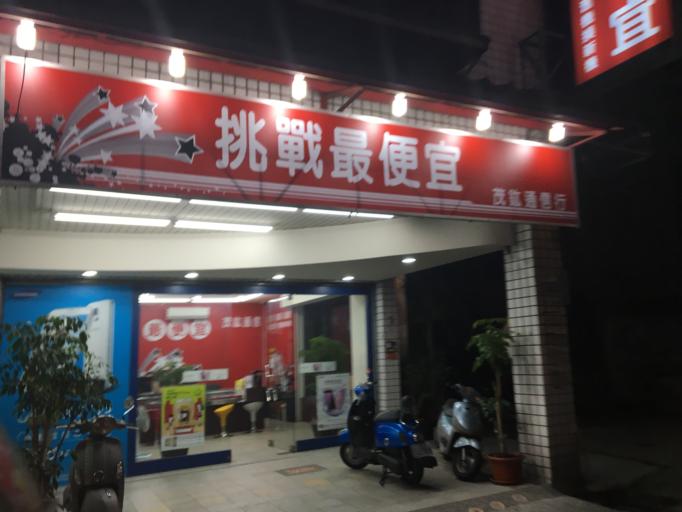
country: TW
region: Taiwan
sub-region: Taichung City
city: Taichung
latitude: 24.1417
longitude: 120.6803
